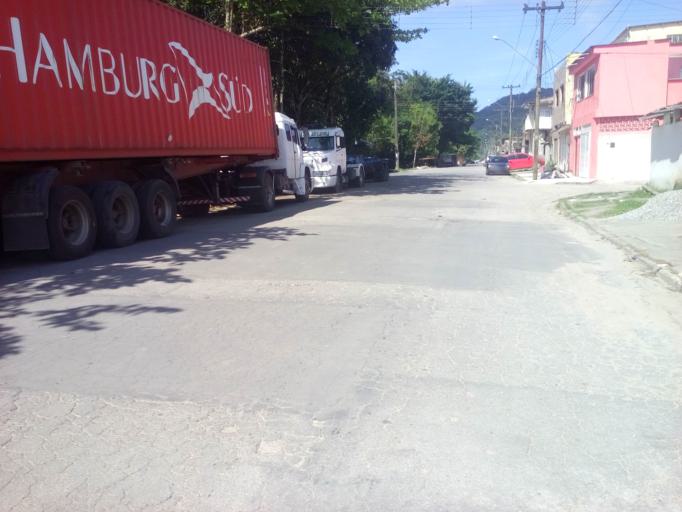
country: BR
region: Sao Paulo
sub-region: Guaruja
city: Guaruja
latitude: -23.9606
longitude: -46.2536
